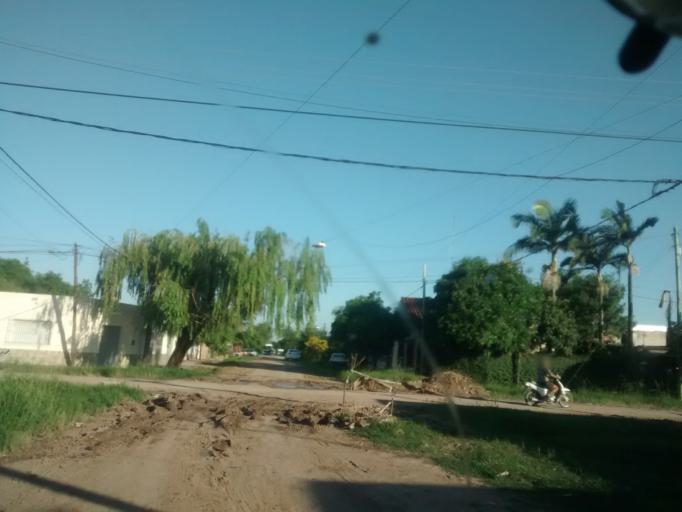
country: AR
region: Chaco
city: Resistencia
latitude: -27.4510
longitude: -59.0098
